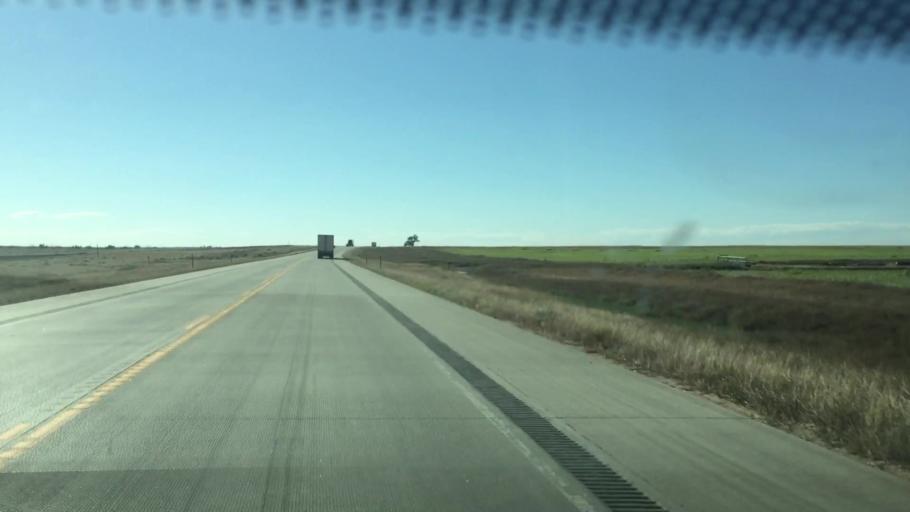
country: US
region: Colorado
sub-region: Kiowa County
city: Eads
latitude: 38.7638
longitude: -102.8179
